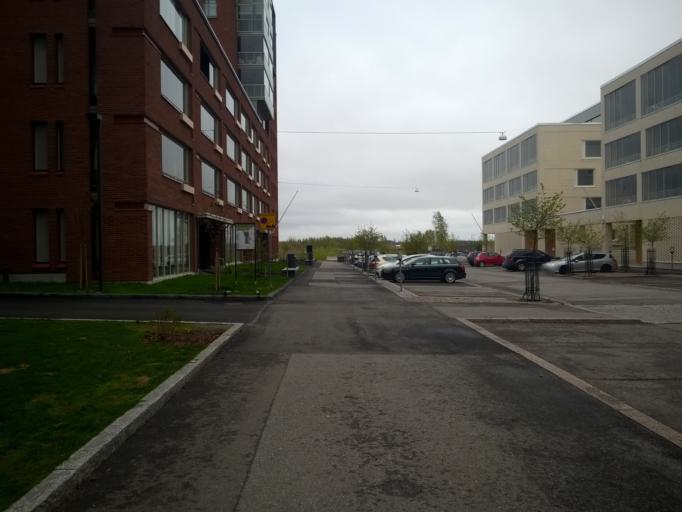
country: FI
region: Uusimaa
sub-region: Helsinki
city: Helsinki
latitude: 60.2027
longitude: 24.9718
